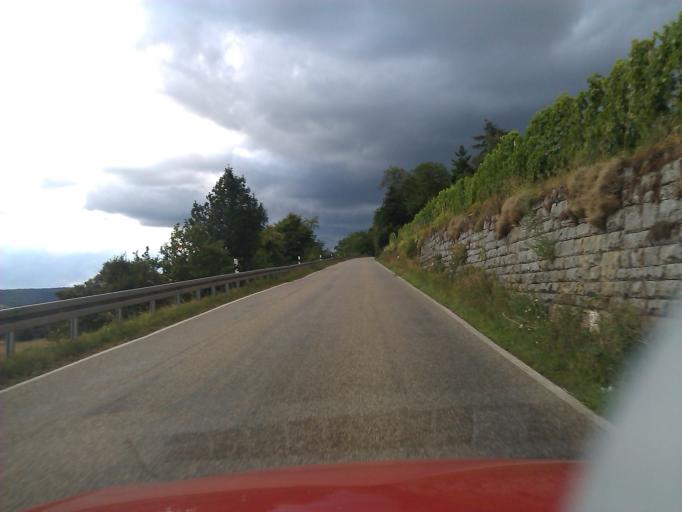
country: DE
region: Baden-Wuerttemberg
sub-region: Regierungsbezirk Stuttgart
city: Guglingen
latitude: 49.0717
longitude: 8.9908
